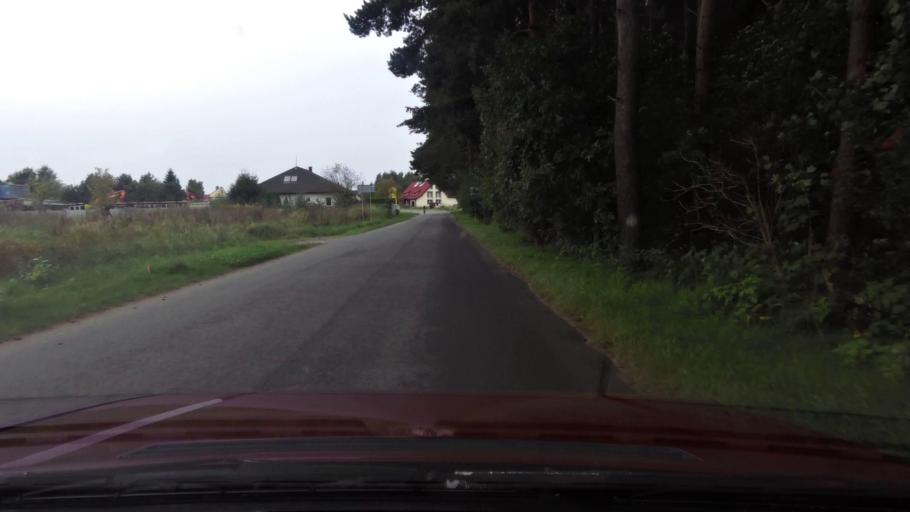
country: PL
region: West Pomeranian Voivodeship
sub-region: Powiat kolobrzeski
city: Grzybowo
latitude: 54.1534
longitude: 15.4990
